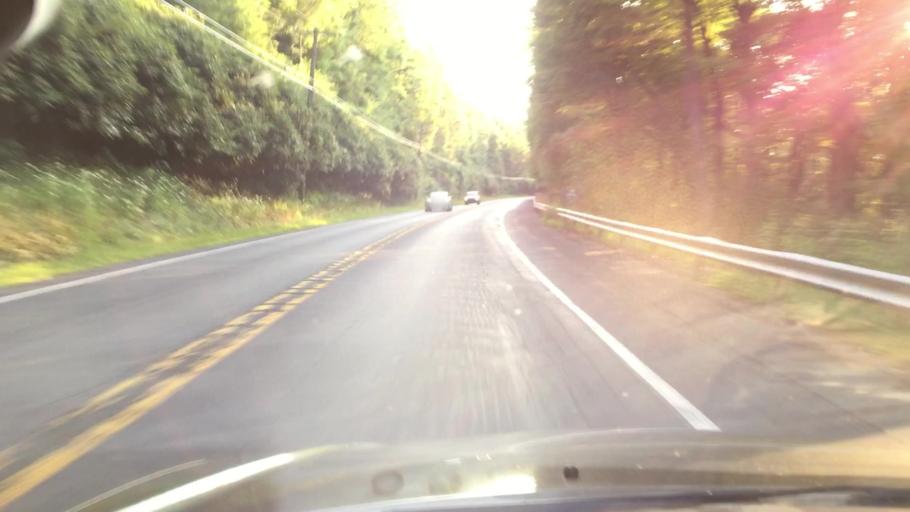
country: US
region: Pennsylvania
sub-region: Carbon County
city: Jim Thorpe
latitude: 40.8718
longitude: -75.7682
